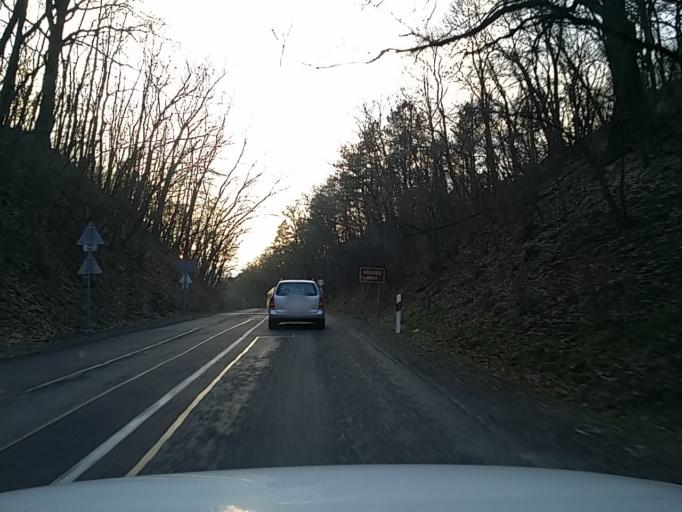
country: HU
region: Nograd
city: Matranovak
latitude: 48.0137
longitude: 20.0273
